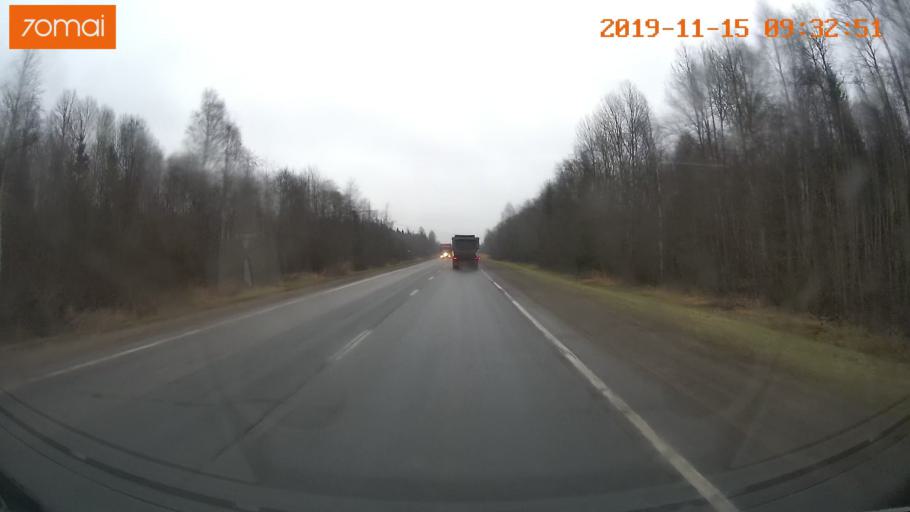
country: RU
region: Vologda
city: Sheksna
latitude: 59.2697
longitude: 38.3451
